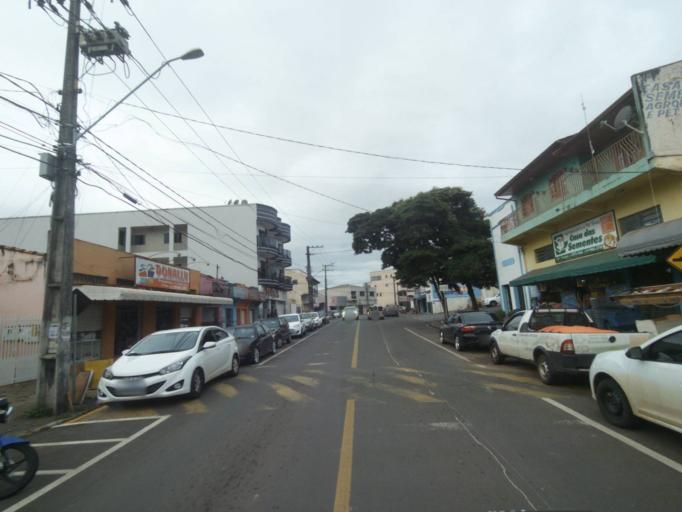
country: BR
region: Parana
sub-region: Telemaco Borba
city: Telemaco Borba
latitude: -24.3295
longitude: -50.6307
